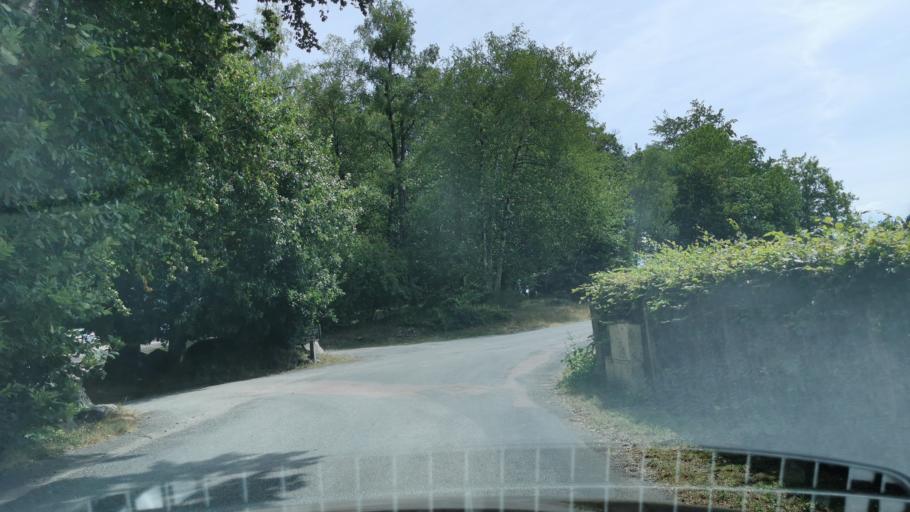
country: FR
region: Bourgogne
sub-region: Departement de Saone-et-Loire
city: Etang-sur-Arroux
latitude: 46.8074
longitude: 4.2605
